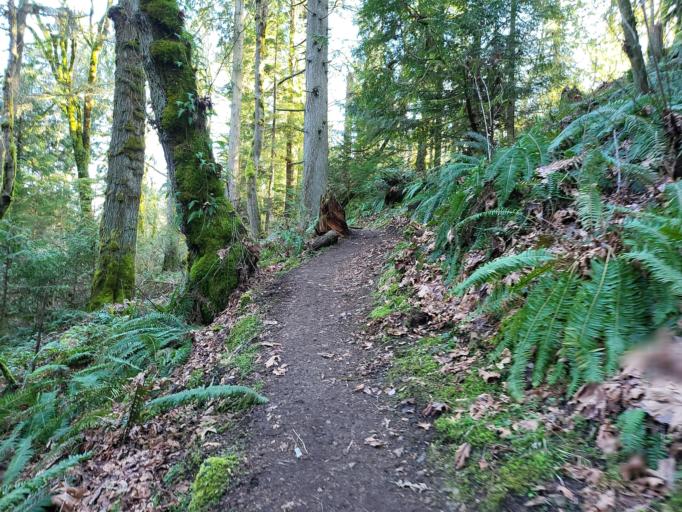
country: US
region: Washington
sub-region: King County
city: East Renton Highlands
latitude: 47.5129
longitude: -122.1207
